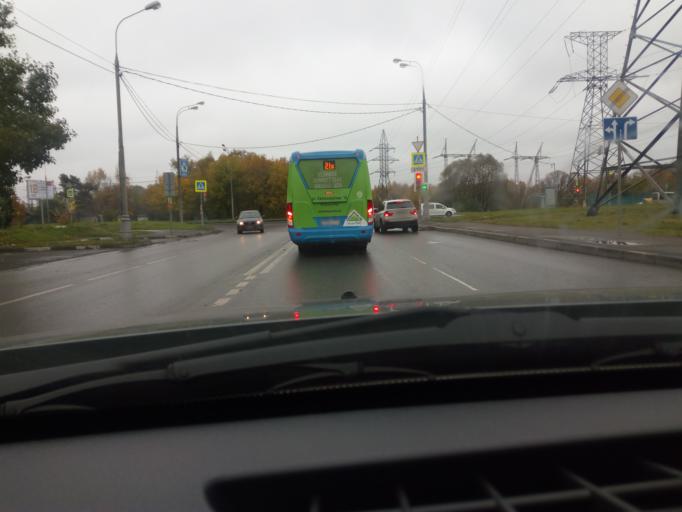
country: RU
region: Moskovskaya
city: Kuskovo
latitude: 55.7320
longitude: 37.8473
